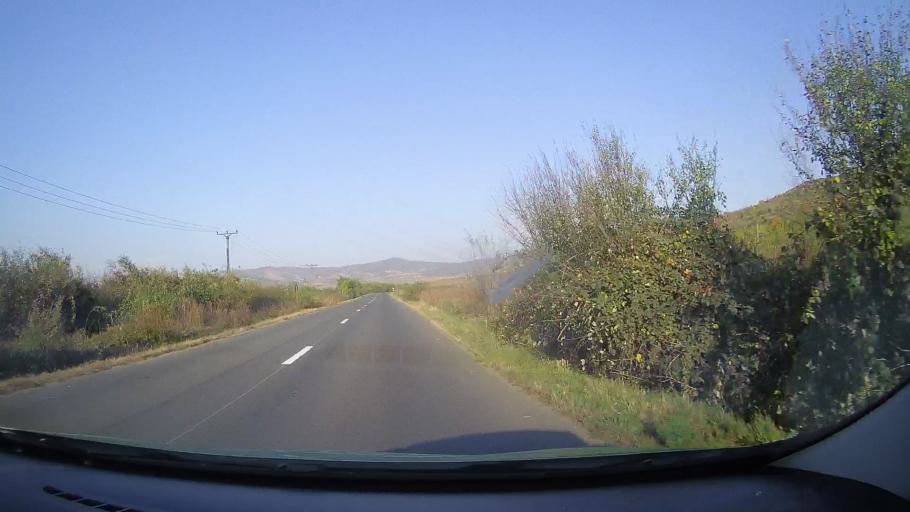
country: RO
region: Arad
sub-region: Comuna Covasint
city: Covasint
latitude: 46.2150
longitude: 21.6161
